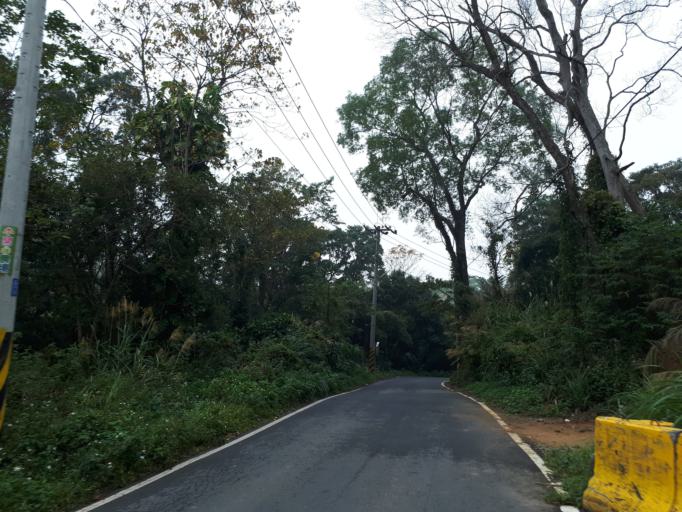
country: TW
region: Taiwan
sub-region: Hsinchu
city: Zhubei
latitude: 24.7345
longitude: 121.0784
